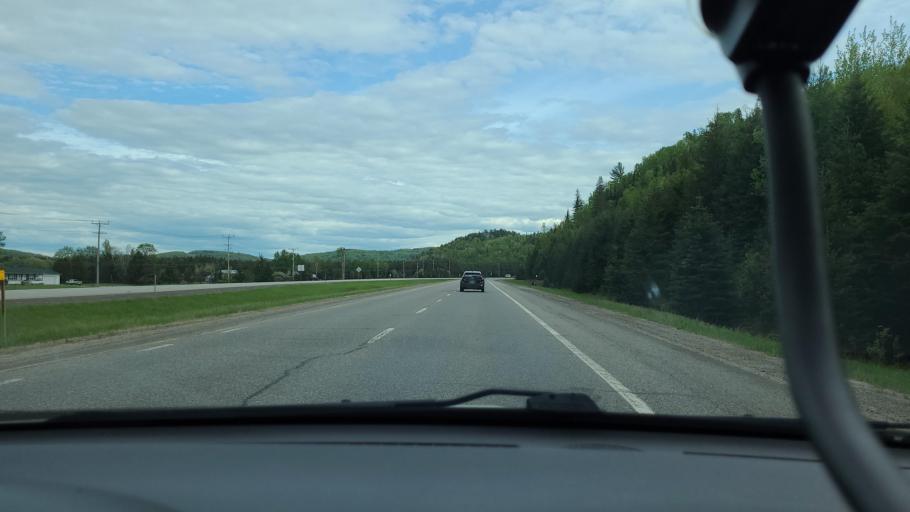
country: CA
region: Quebec
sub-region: Laurentides
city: Labelle
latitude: 46.2251
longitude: -74.7129
